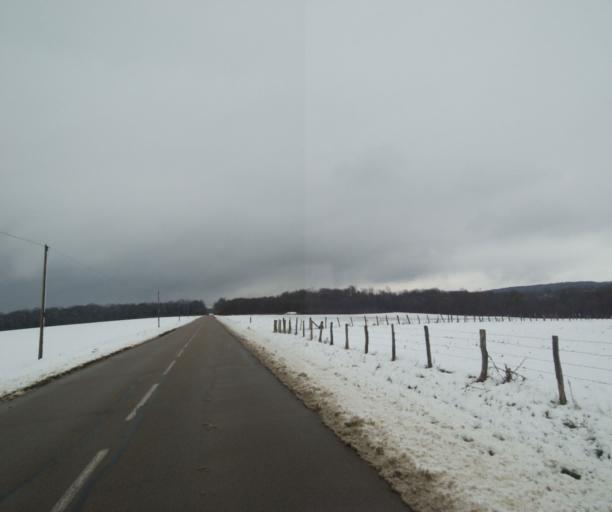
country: FR
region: Champagne-Ardenne
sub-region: Departement de la Haute-Marne
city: Laneuville-a-Remy
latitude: 48.4236
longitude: 4.8427
